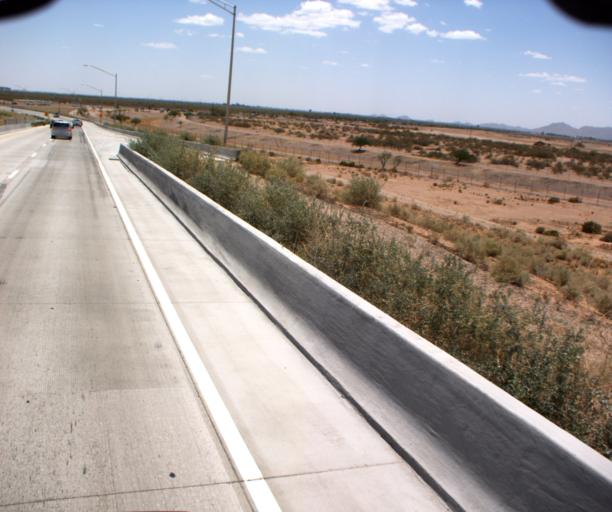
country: US
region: Arizona
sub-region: Maricopa County
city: Queen Creek
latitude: 33.3186
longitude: -111.6397
